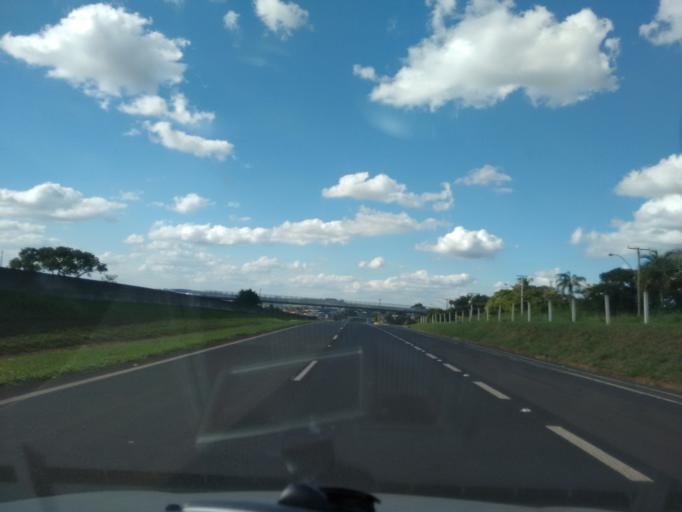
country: BR
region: Sao Paulo
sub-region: Araraquara
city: Araraquara
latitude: -21.8115
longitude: -48.1553
